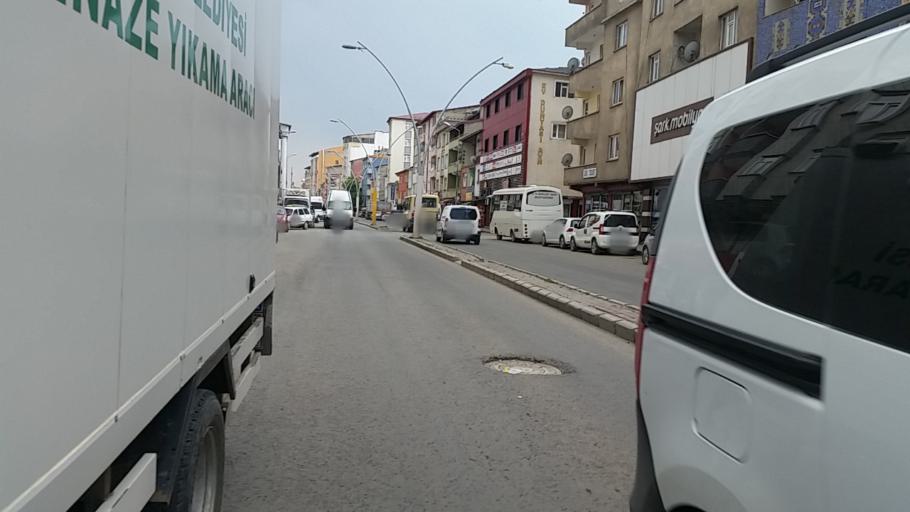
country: TR
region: Agri
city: Agri
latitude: 39.7241
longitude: 43.0514
